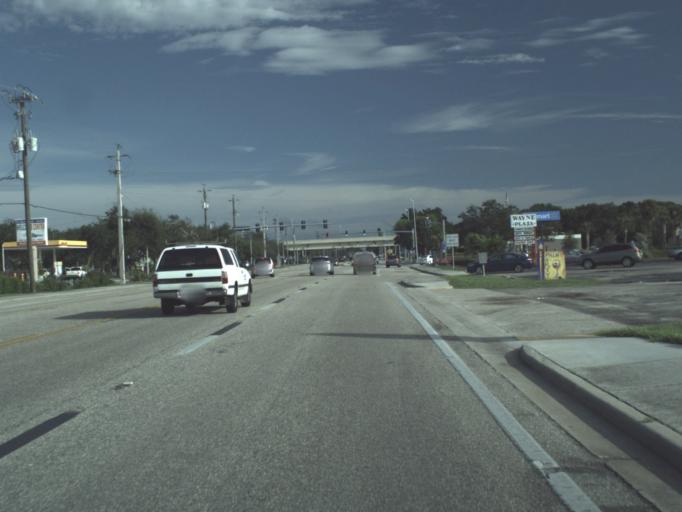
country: US
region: Florida
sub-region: Lee County
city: Harlem Heights
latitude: 26.4905
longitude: -81.9431
